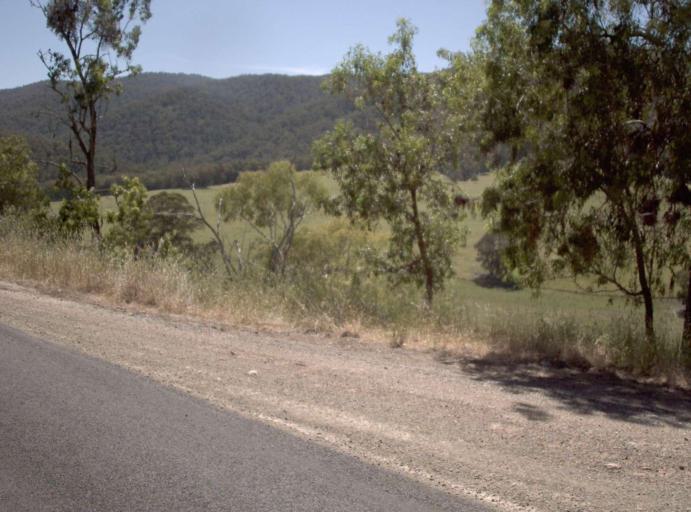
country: AU
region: Victoria
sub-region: East Gippsland
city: Lakes Entrance
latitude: -37.4119
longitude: 148.2093
